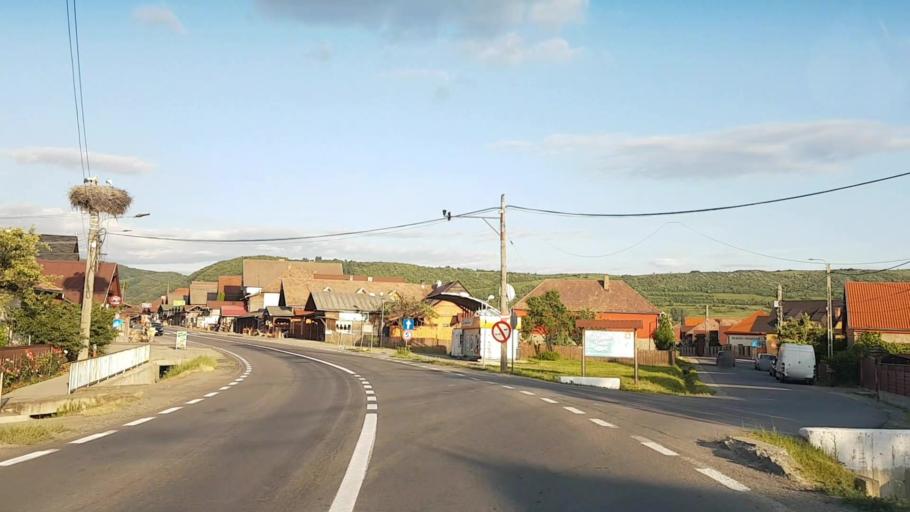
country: RO
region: Harghita
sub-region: Comuna Corund
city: Corund
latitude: 46.4740
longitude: 25.1784
